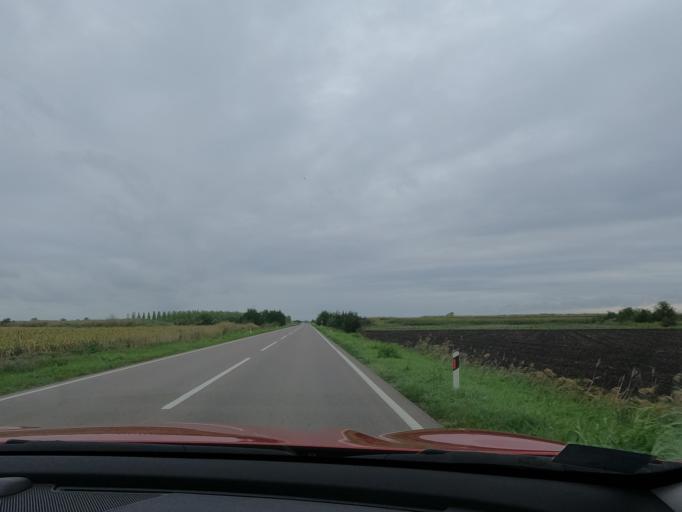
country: RS
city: Basaid
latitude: 45.6617
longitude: 20.4210
